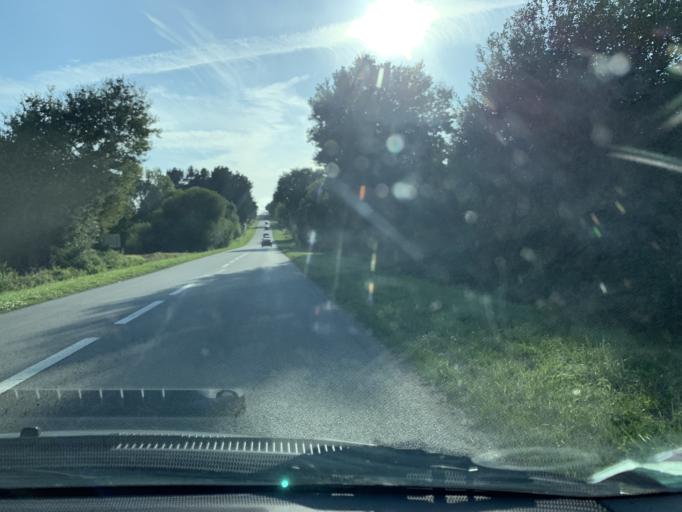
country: FR
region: Brittany
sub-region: Departement du Morbihan
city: Surzur
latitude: 47.5754
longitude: -2.6305
